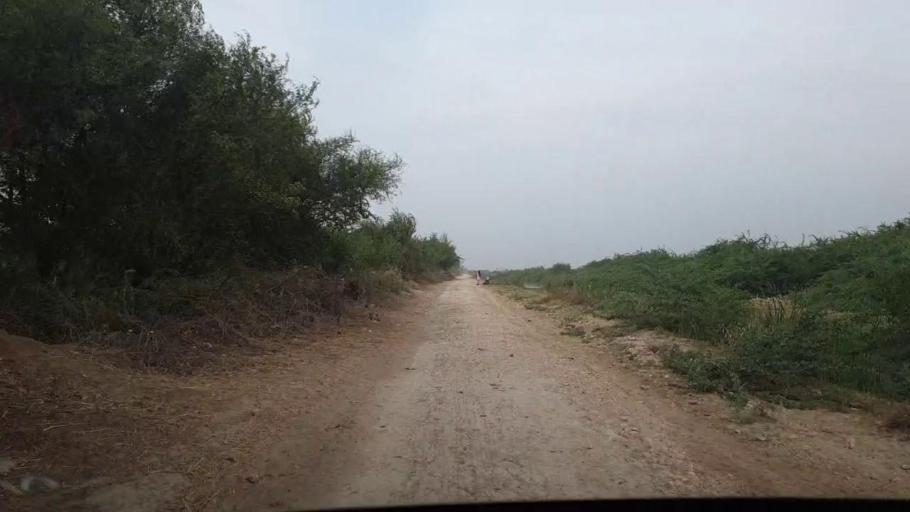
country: PK
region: Sindh
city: Chuhar Jamali
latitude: 24.4079
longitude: 67.9523
